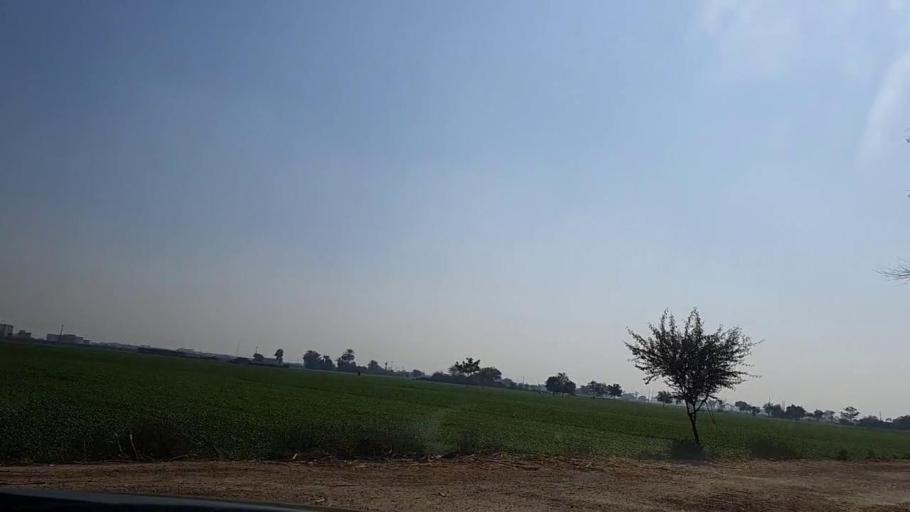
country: PK
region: Sindh
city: Nawabshah
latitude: 26.2278
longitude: 68.3148
